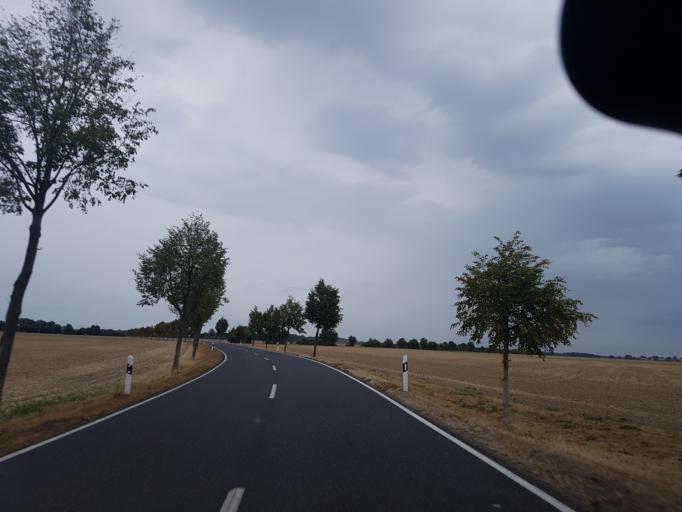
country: DE
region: Saxony-Anhalt
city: Pretzsch
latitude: 51.7364
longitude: 12.8815
